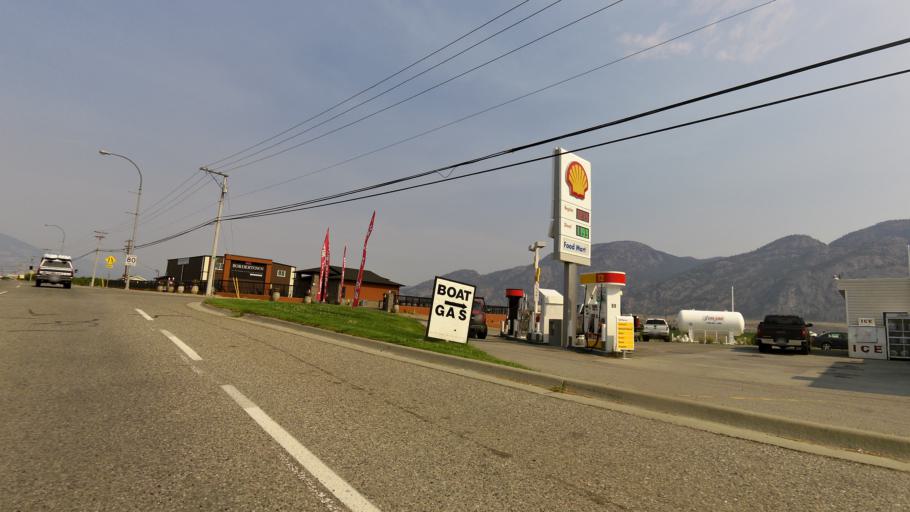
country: CA
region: British Columbia
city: Osoyoos
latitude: 49.0367
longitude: -119.4776
